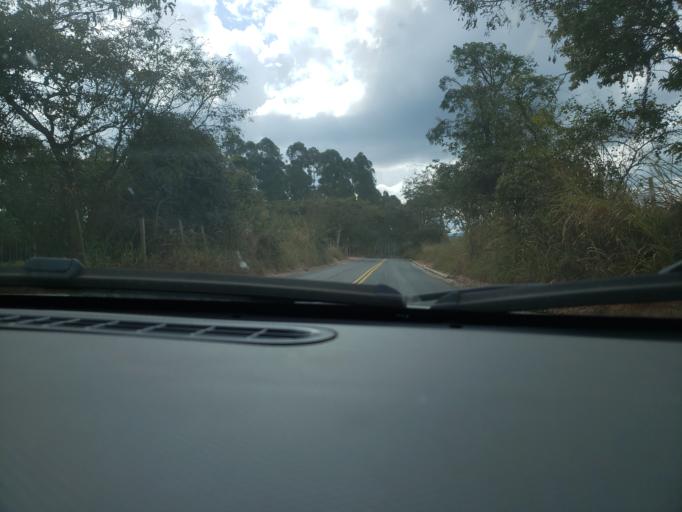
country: BR
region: Minas Gerais
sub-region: Campo Belo
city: Campo Belo
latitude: -20.9154
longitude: -45.2935
